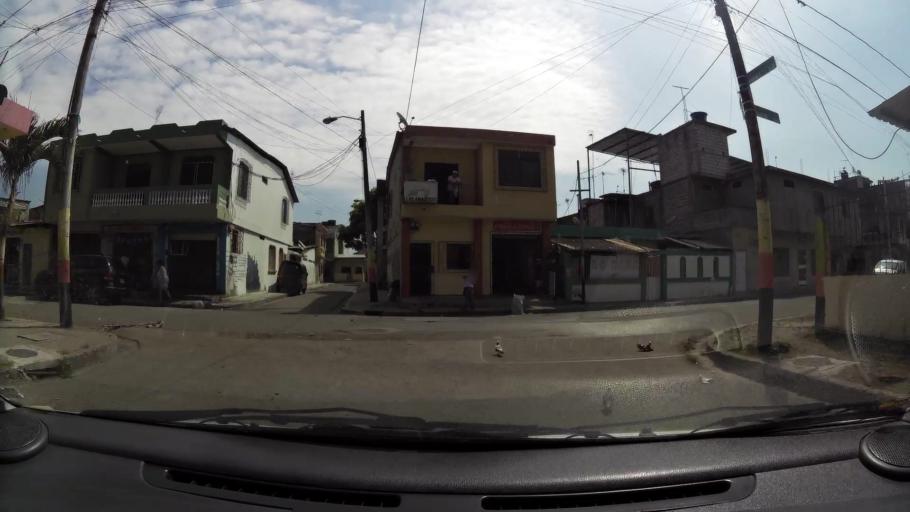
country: EC
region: Guayas
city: Guayaquil
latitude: -2.2553
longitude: -79.8917
